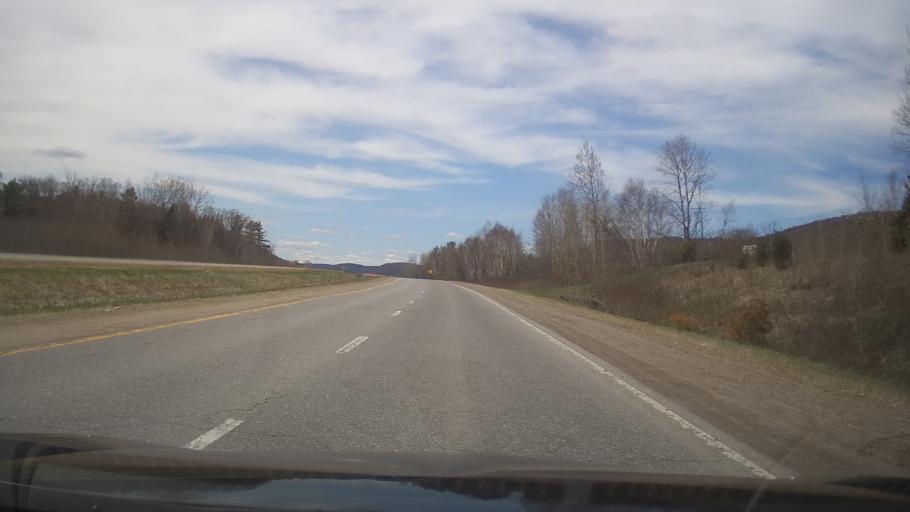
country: CA
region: Quebec
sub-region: Outaouais
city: Wakefield
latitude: 45.5318
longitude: -76.0068
